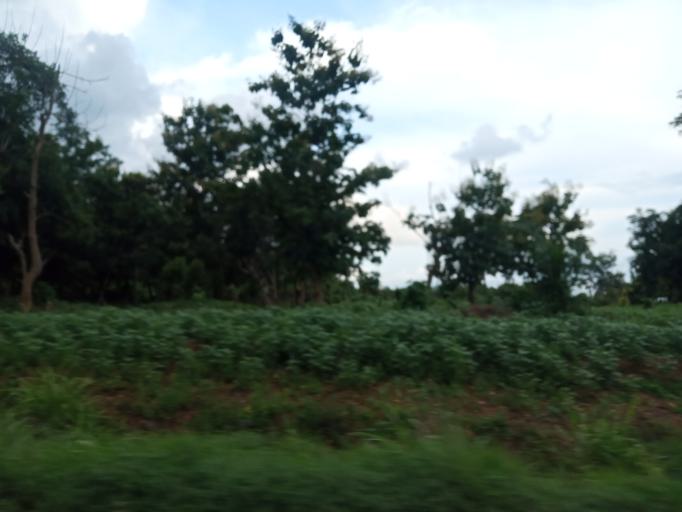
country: TG
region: Centrale
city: Sotouboua
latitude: 8.5851
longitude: 0.9877
